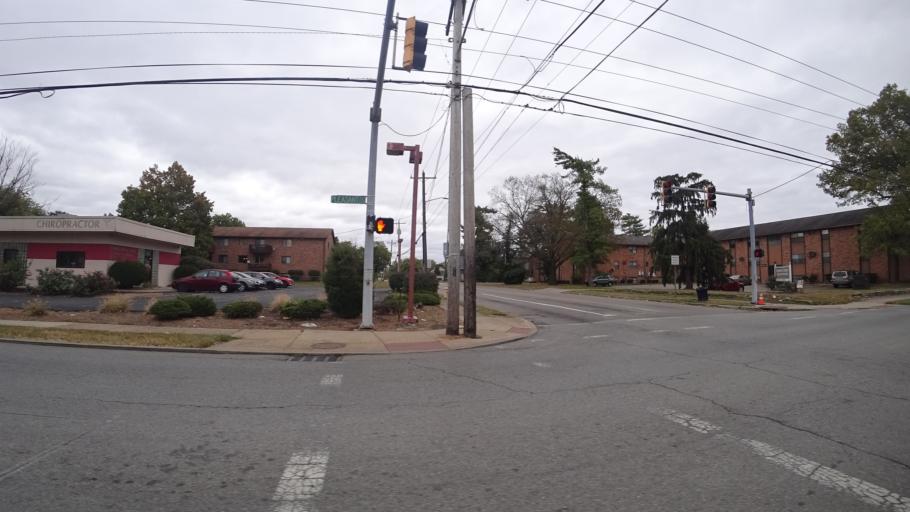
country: US
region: Ohio
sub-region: Butler County
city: Fairfield
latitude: 39.3594
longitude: -84.5583
